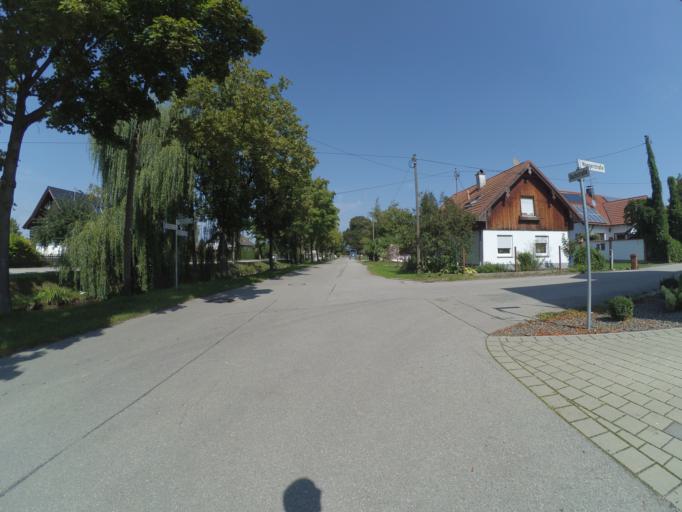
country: DE
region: Bavaria
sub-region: Swabia
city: Lamerdingen
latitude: 48.0926
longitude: 10.7376
